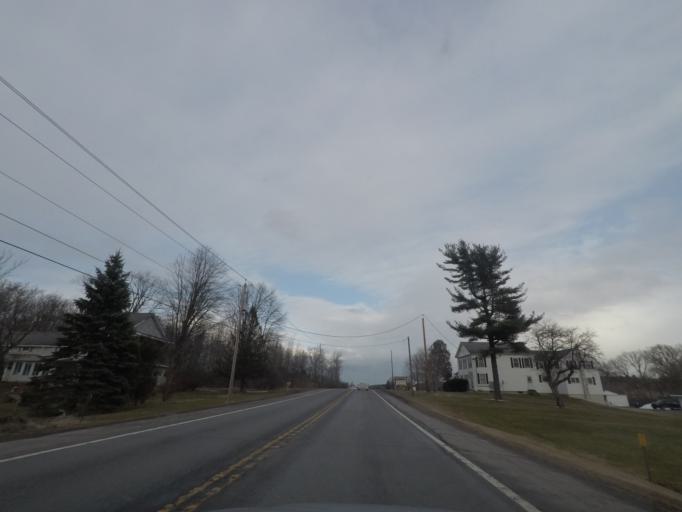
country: US
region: New York
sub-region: Oneida County
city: Vernon
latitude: 43.0746
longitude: -75.4638
